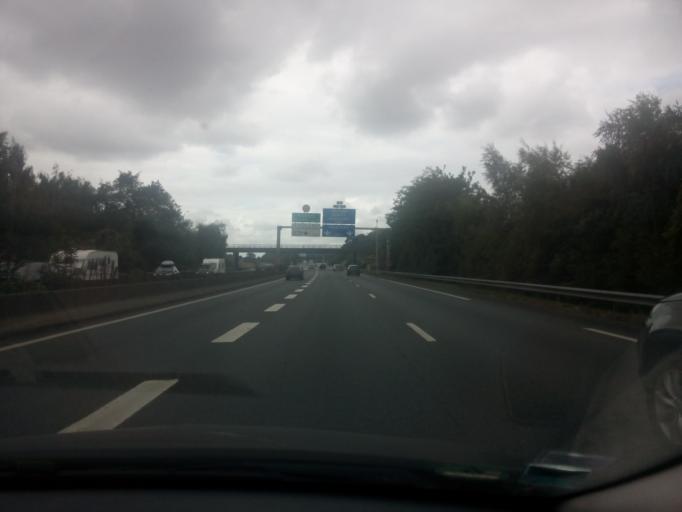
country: FR
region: Ile-de-France
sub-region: Departement de l'Essonne
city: Massy
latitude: 48.7198
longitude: 2.2936
